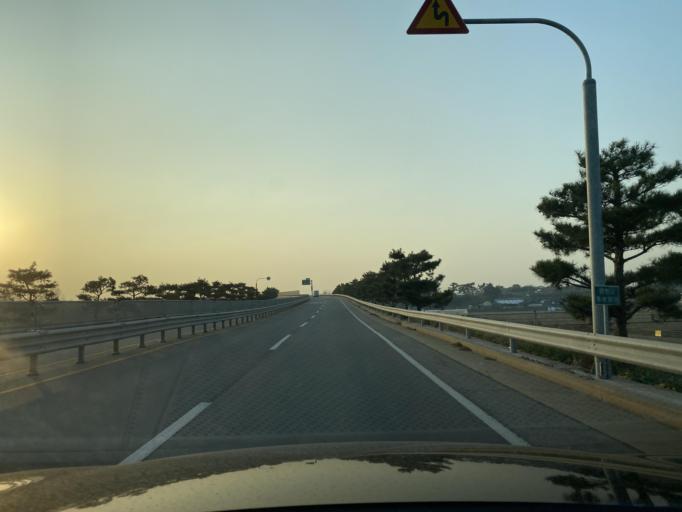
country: KR
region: Chungcheongnam-do
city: Yesan
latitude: 36.6969
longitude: 126.8006
